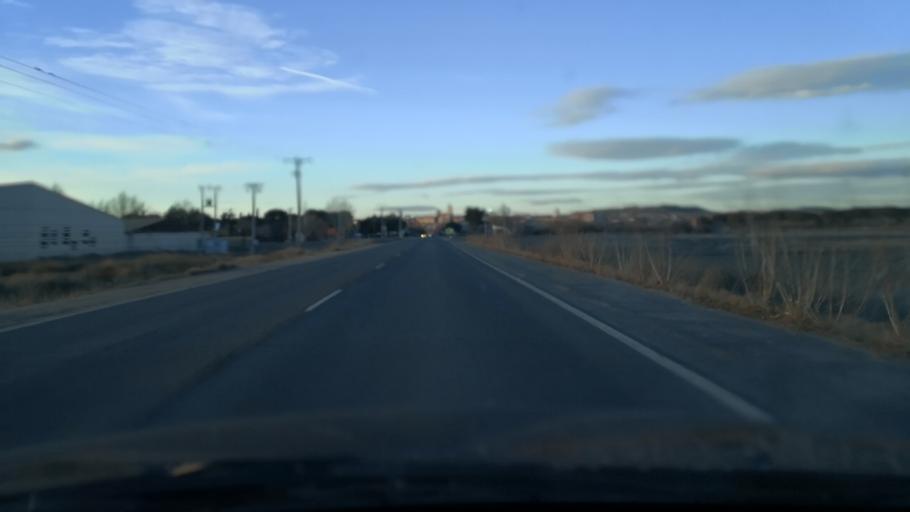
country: ES
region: Castille and Leon
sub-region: Provincia de Valladolid
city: Tordesillas
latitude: 41.4864
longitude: -4.9952
